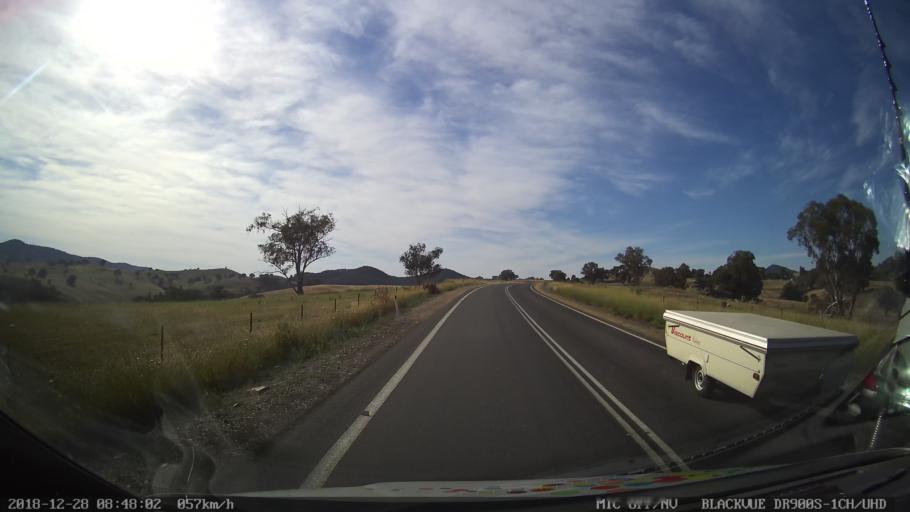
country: AU
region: New South Wales
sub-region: Upper Lachlan Shire
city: Crookwell
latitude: -34.0321
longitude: 149.3362
